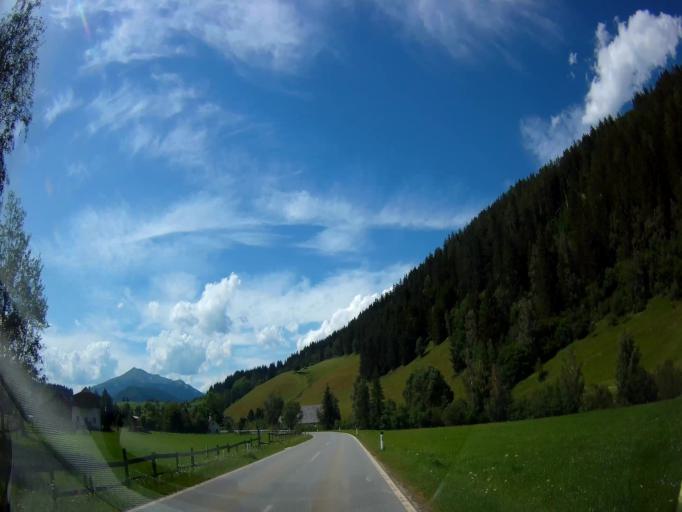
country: AT
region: Salzburg
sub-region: Politischer Bezirk Tamsweg
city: Thomatal
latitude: 47.0769
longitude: 13.7389
